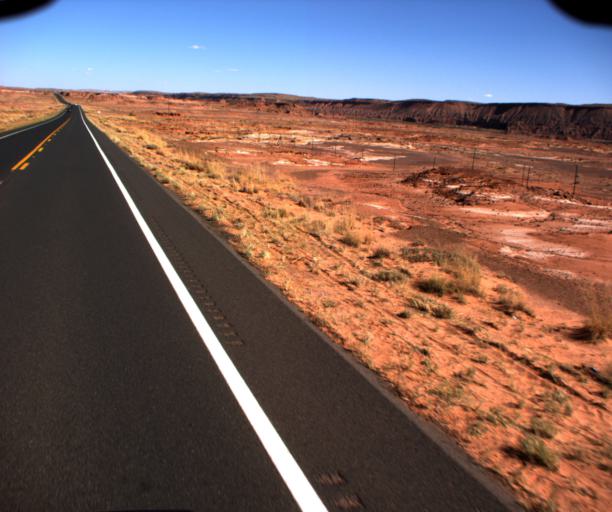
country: US
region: Arizona
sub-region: Coconino County
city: Tuba City
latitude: 36.1014
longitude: -111.3026
